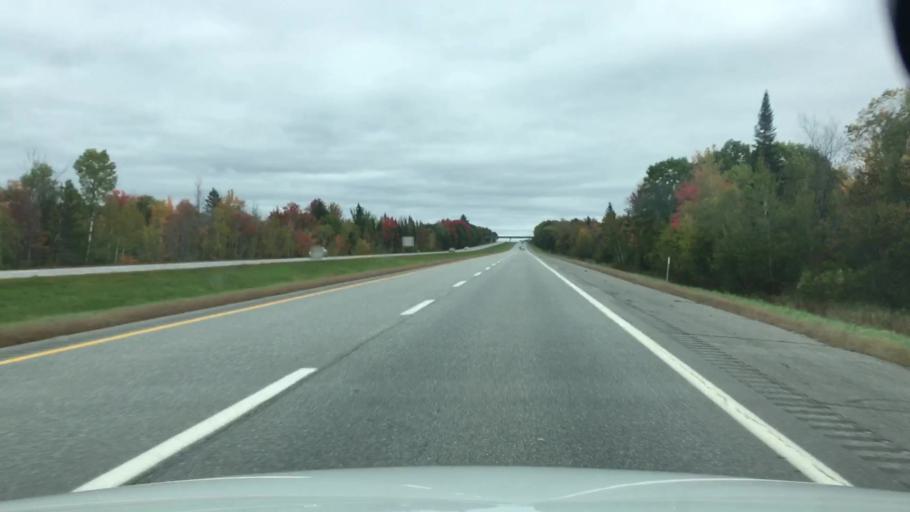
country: US
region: Maine
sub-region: Penobscot County
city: Newport
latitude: 44.8237
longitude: -69.2705
